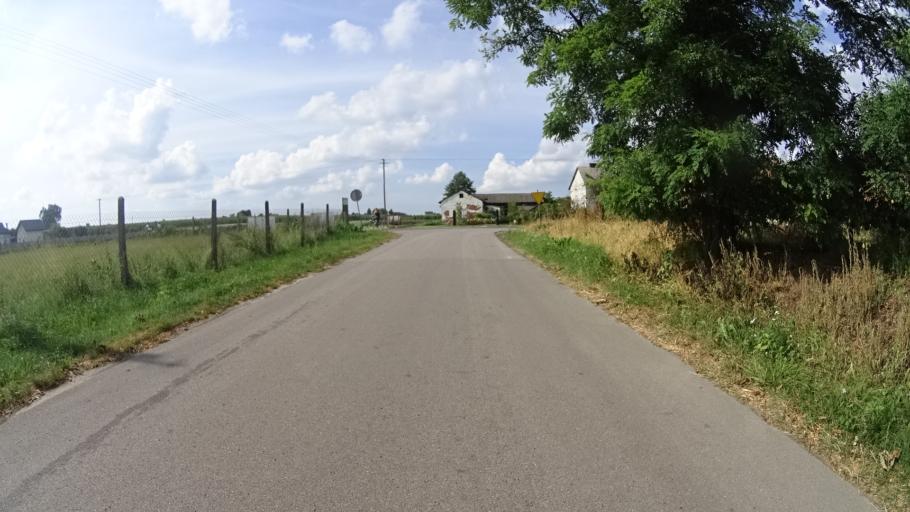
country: PL
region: Masovian Voivodeship
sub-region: Powiat grojecki
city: Goszczyn
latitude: 51.7008
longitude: 20.8467
